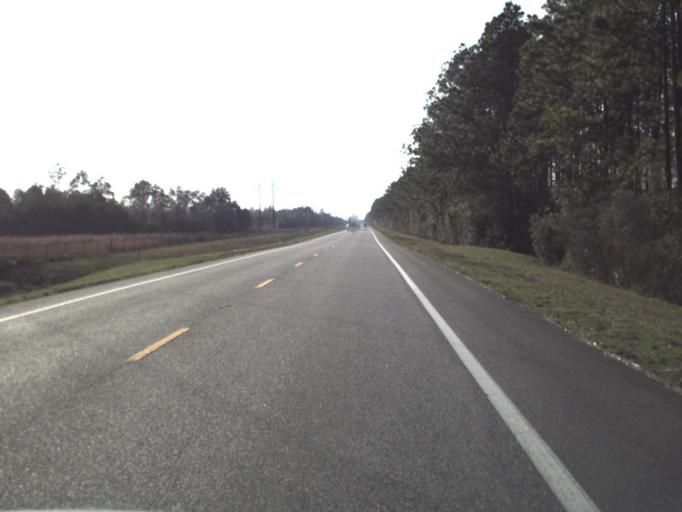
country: US
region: Florida
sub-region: Bay County
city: Lynn Haven
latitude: 30.4398
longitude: -85.7829
